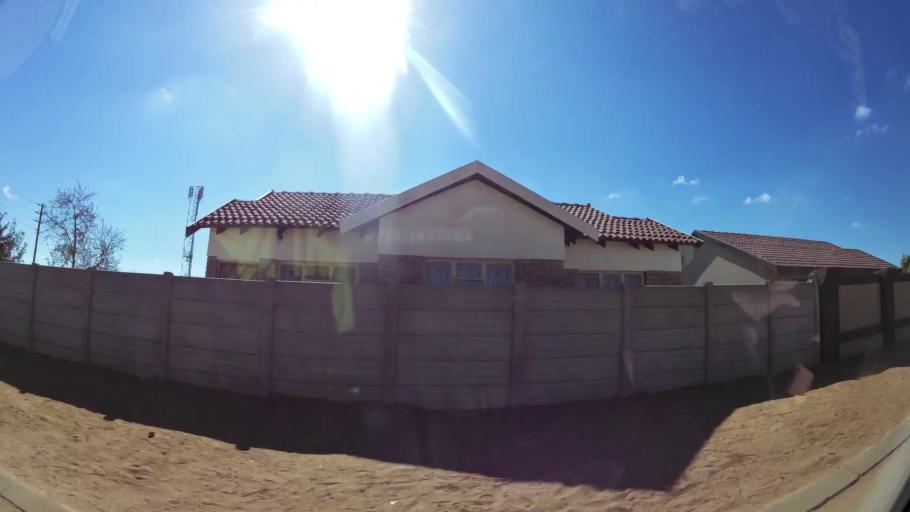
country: ZA
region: Limpopo
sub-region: Capricorn District Municipality
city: Polokwane
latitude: -23.8760
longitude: 29.4108
